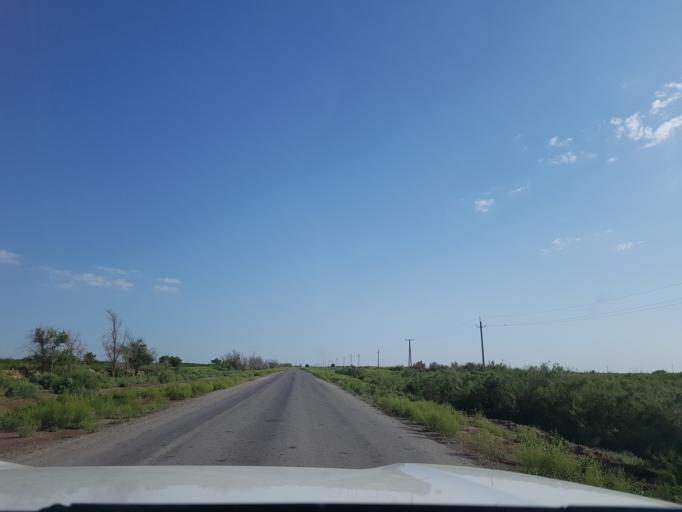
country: TM
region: Dasoguz
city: Koeneuergench
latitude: 41.8880
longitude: 58.7068
